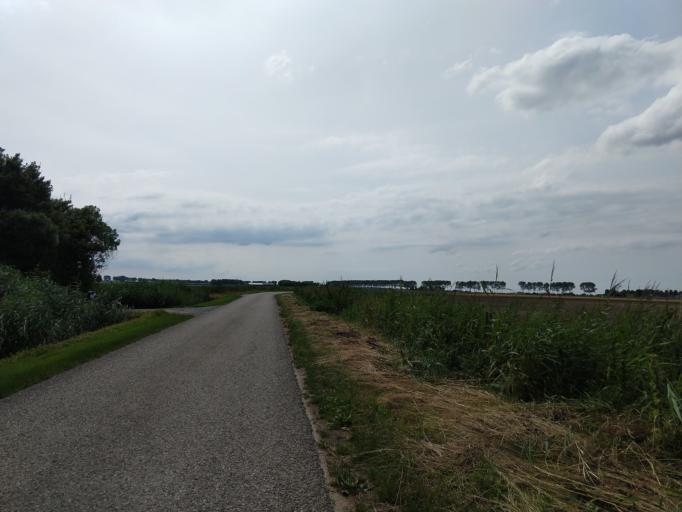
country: NL
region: North Brabant
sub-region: Gemeente Steenbergen
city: Dinteloord
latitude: 51.6744
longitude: 4.3453
